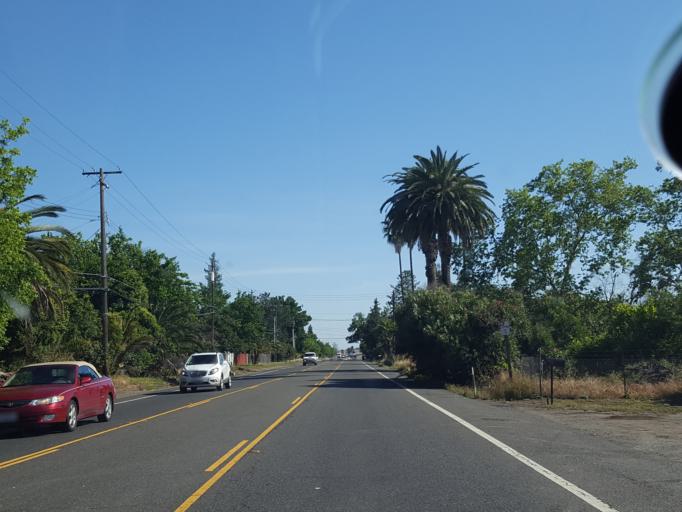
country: US
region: California
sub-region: Sacramento County
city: Florin
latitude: 38.4913
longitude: -121.3905
